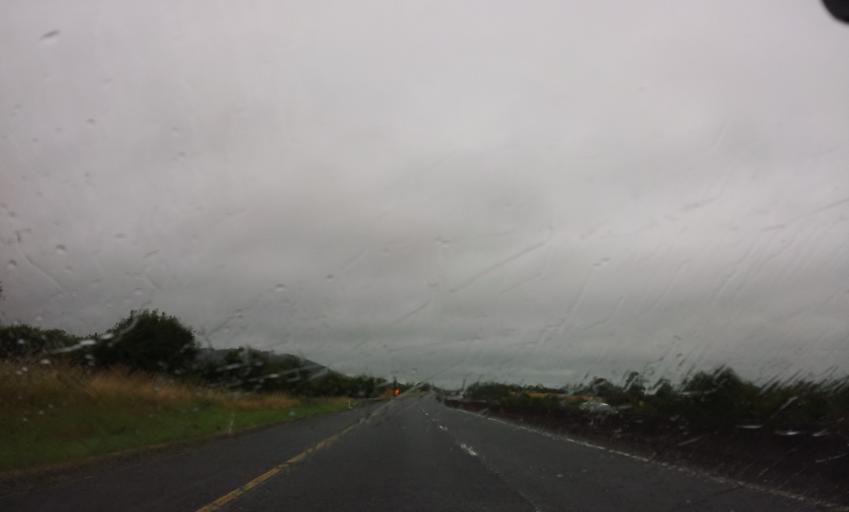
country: IE
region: Munster
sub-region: County Cork
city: Rathcormac
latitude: 52.0899
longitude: -8.2919
